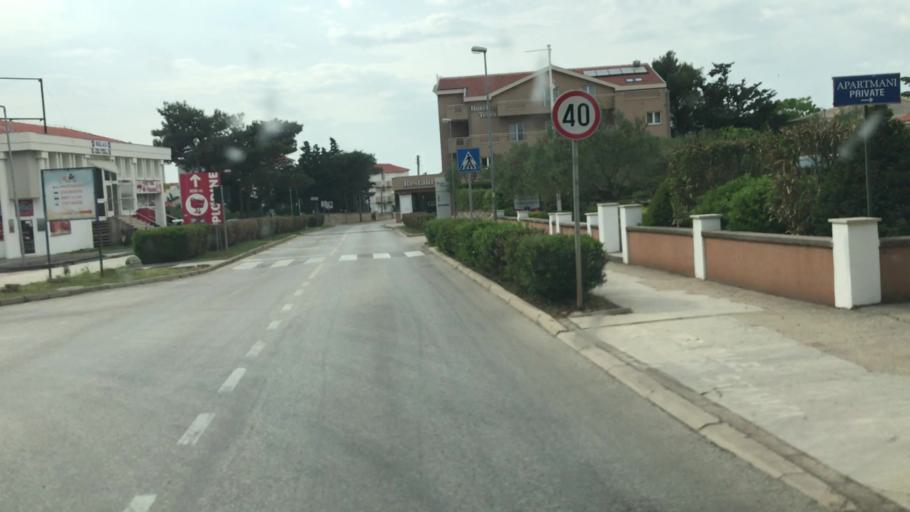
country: HR
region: Licko-Senjska
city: Novalja
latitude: 44.5470
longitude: 14.8866
